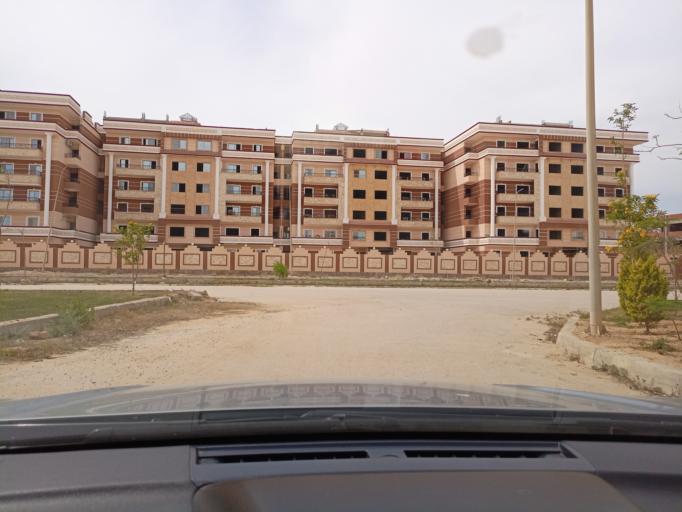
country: EG
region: Muhafazat al Qalyubiyah
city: Al Khankah
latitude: 30.2471
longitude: 31.5015
